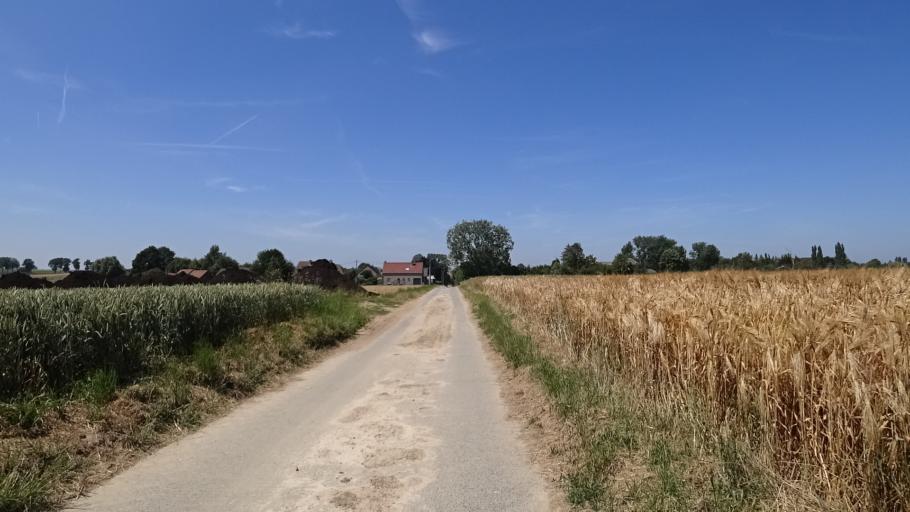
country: BE
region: Wallonia
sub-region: Province du Brabant Wallon
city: Incourt
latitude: 50.6675
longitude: 4.8348
